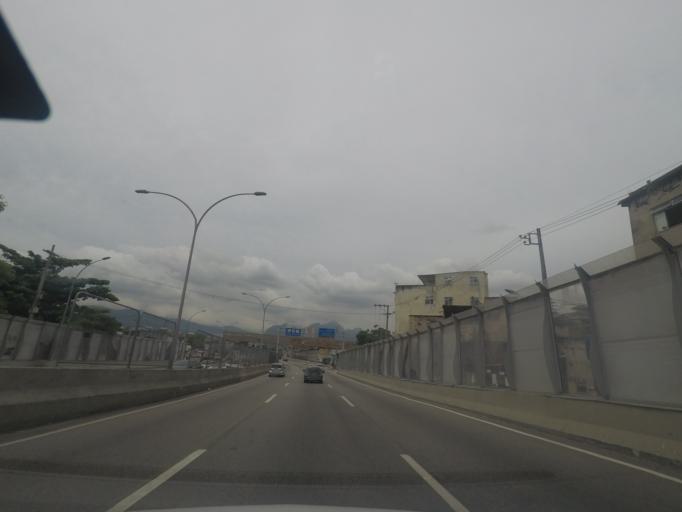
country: BR
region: Rio de Janeiro
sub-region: Rio De Janeiro
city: Rio de Janeiro
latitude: -22.8631
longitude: -43.2391
